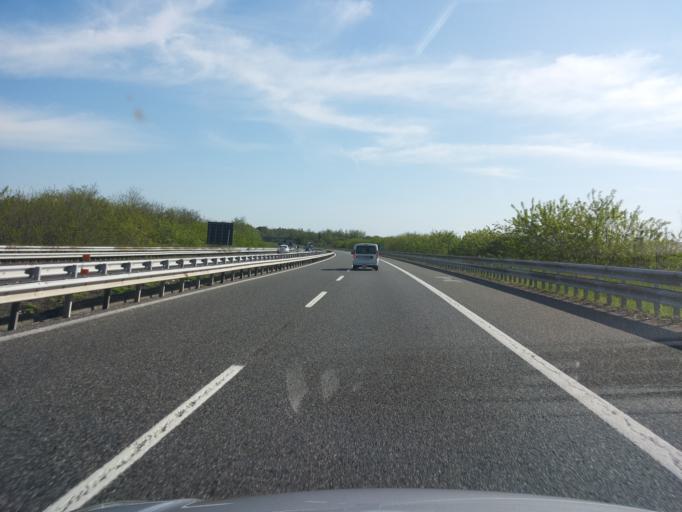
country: IT
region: Piedmont
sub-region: Provincia di Novara
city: Ghemme
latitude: 45.6028
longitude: 8.4031
